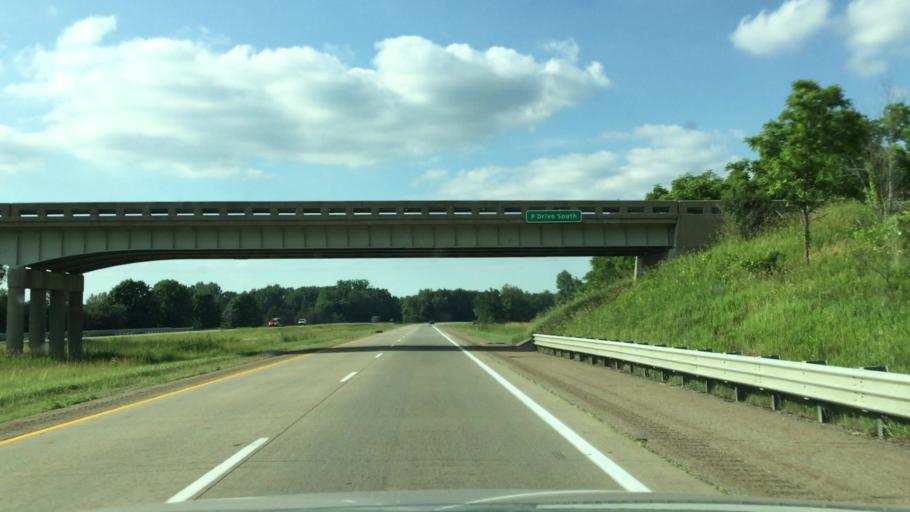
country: US
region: Michigan
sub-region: Calhoun County
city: Marshall
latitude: 42.1309
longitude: -84.9952
